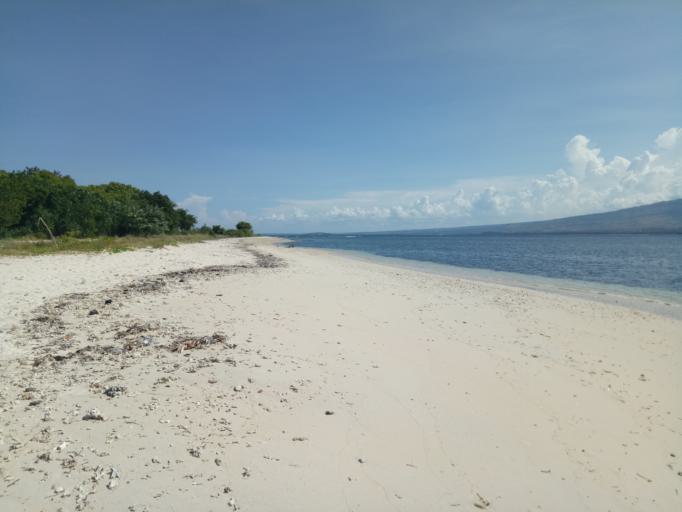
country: ID
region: West Nusa Tenggara
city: Sambelia
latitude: -8.4428
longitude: 116.7327
